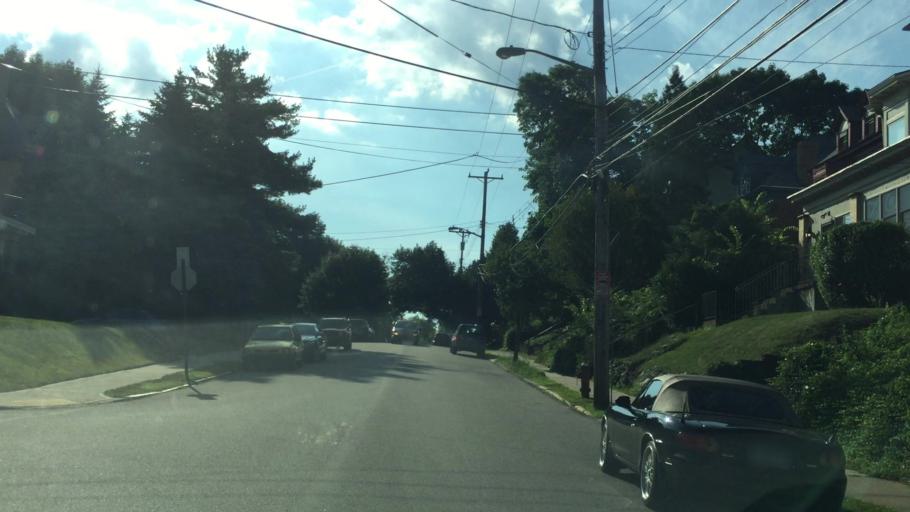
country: US
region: Pennsylvania
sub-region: Allegheny County
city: Homestead
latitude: 40.4369
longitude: -79.9177
